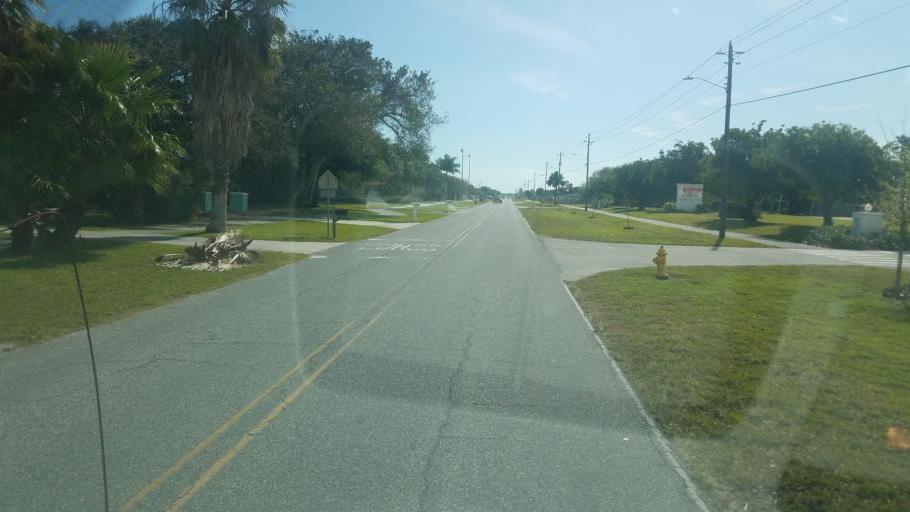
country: US
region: Florida
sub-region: Brevard County
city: Melbourne Beach
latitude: 28.0578
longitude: -80.5582
